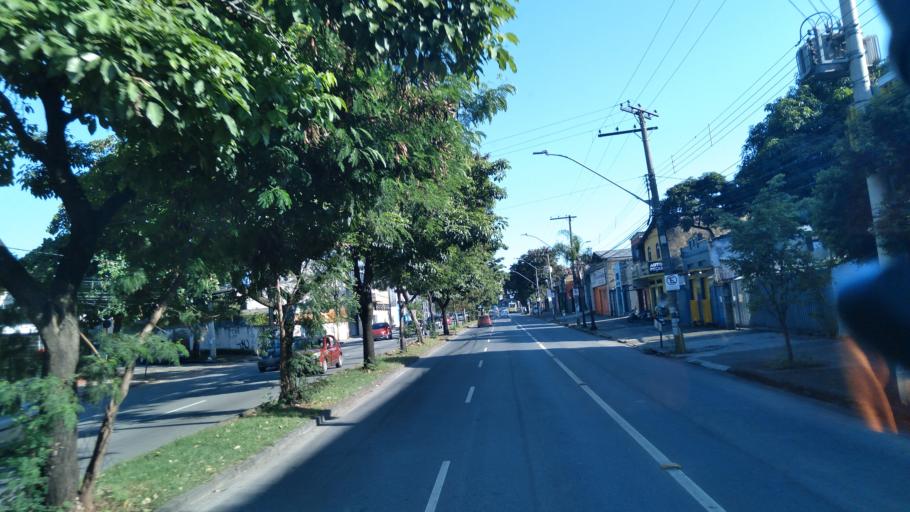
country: BR
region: Minas Gerais
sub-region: Belo Horizonte
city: Belo Horizonte
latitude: -19.9096
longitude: -43.9822
